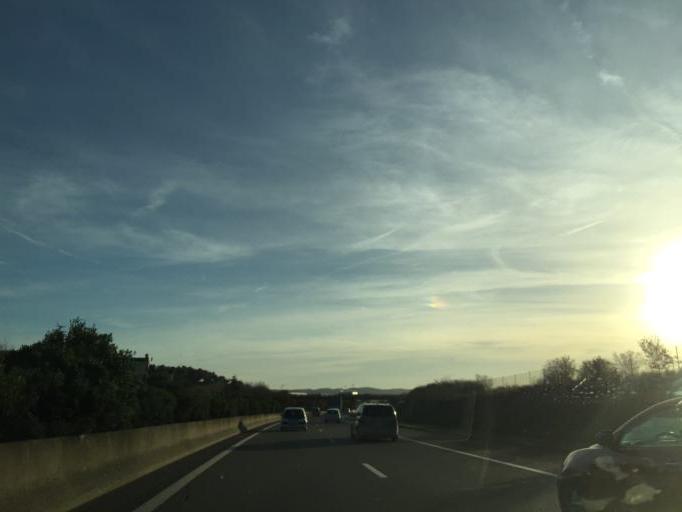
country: FR
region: Rhone-Alpes
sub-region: Departement du Rhone
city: Corbas
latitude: 45.6512
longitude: 4.9196
